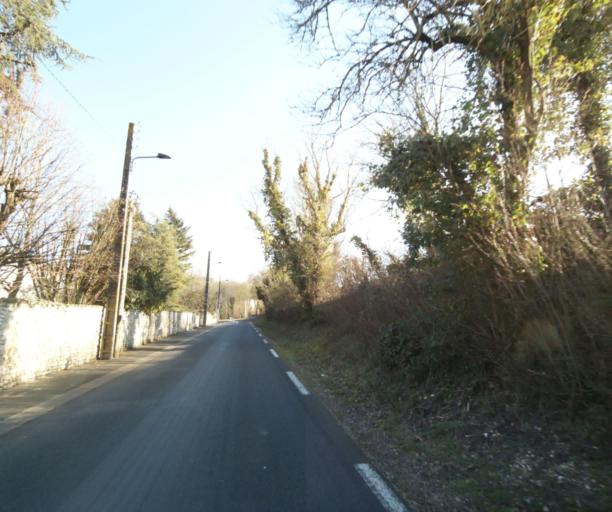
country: FR
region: Poitou-Charentes
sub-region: Departement des Deux-Sevres
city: Niort
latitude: 46.3364
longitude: -0.4391
